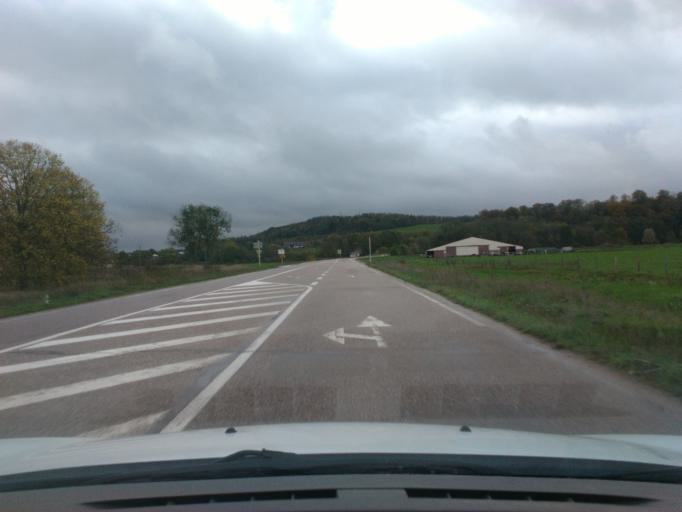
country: FR
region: Lorraine
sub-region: Departement des Vosges
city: Charmes
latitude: 48.3774
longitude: 6.2704
